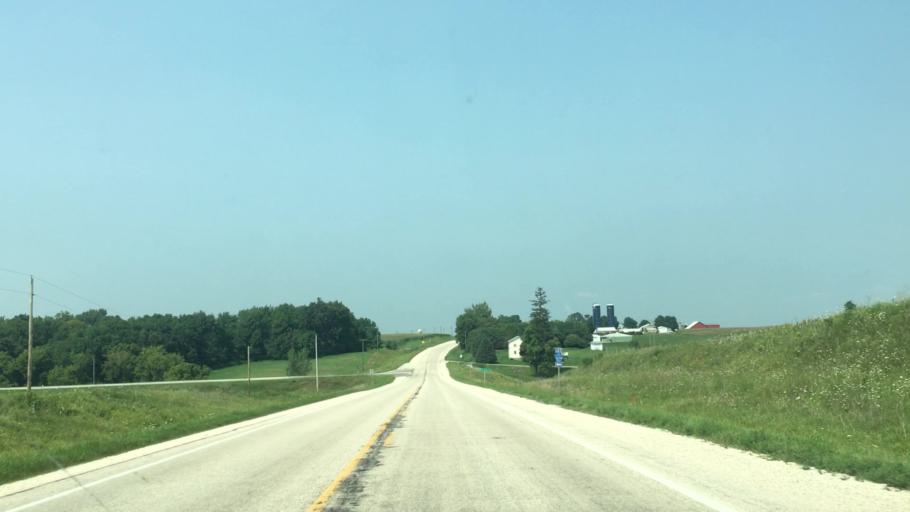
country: US
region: Iowa
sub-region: Fayette County
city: West Union
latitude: 43.0015
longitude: -91.8243
